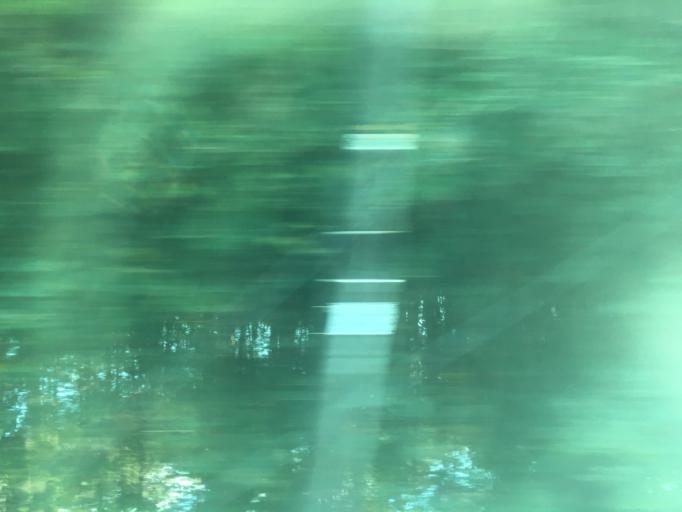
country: JP
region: Ibaraki
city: Tomobe
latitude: 36.3132
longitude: 140.2897
